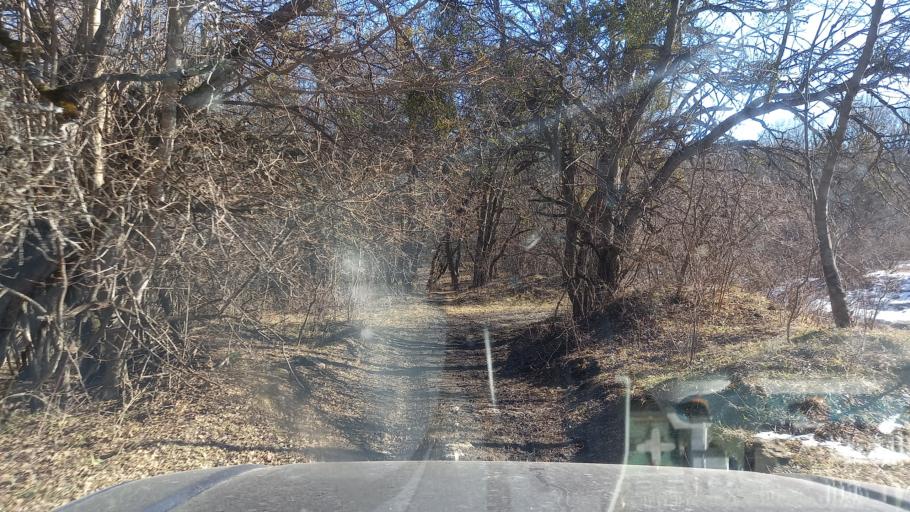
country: RU
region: Adygeya
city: Kamennomostskiy
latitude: 44.2803
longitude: 40.3263
